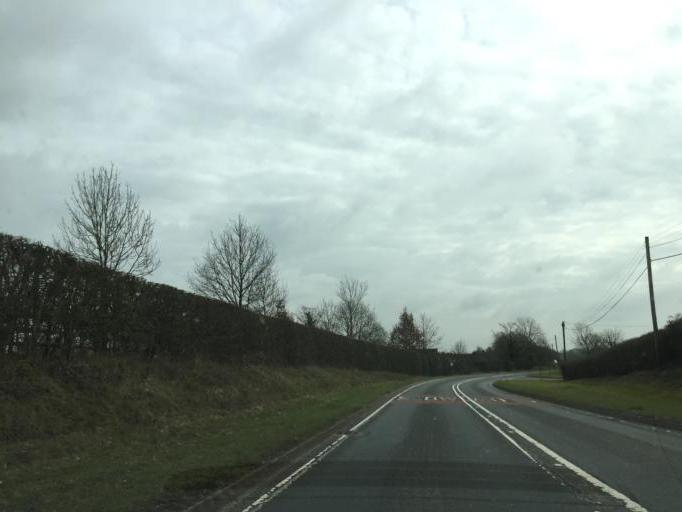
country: GB
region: England
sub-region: Warwickshire
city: Henley in Arden
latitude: 52.2927
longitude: -1.8250
